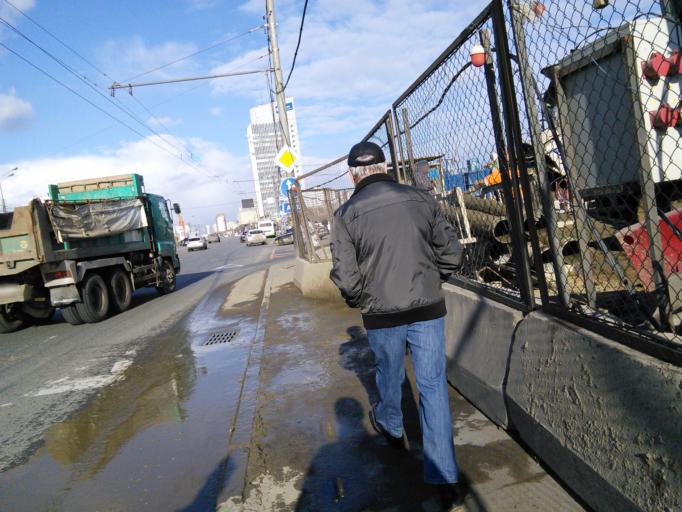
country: RU
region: Moskovskaya
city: Bogorodskoye
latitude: 55.8017
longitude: 37.7494
